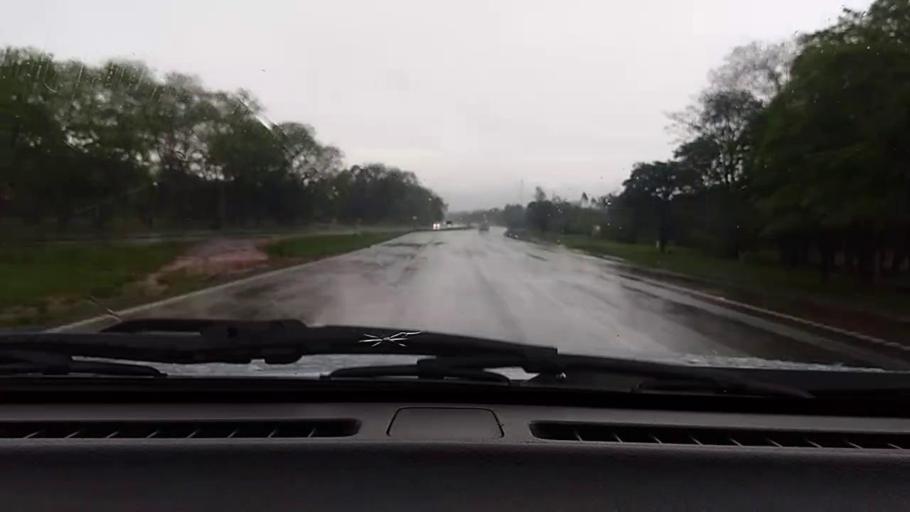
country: PY
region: Caaguazu
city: Repatriacion
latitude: -25.4547
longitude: -55.9116
